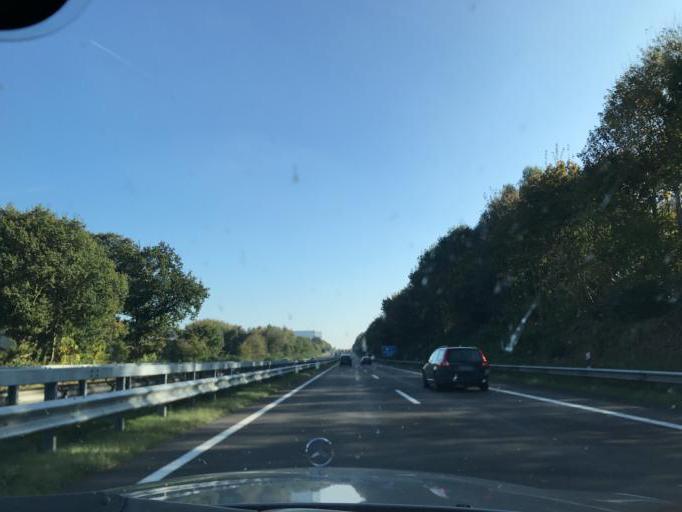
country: DE
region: Lower Saxony
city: Westerstede
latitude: 53.2692
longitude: 7.9262
